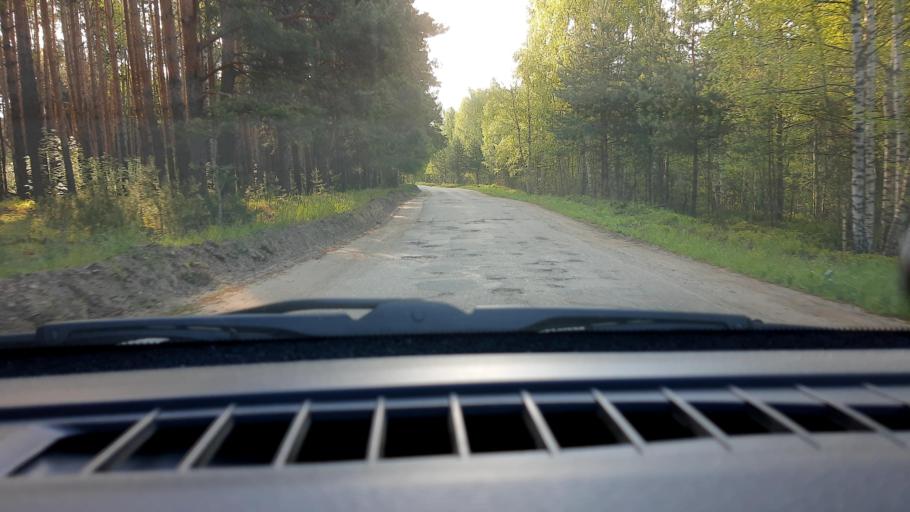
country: RU
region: Nizjnij Novgorod
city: Sitniki
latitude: 56.4150
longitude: 44.0510
